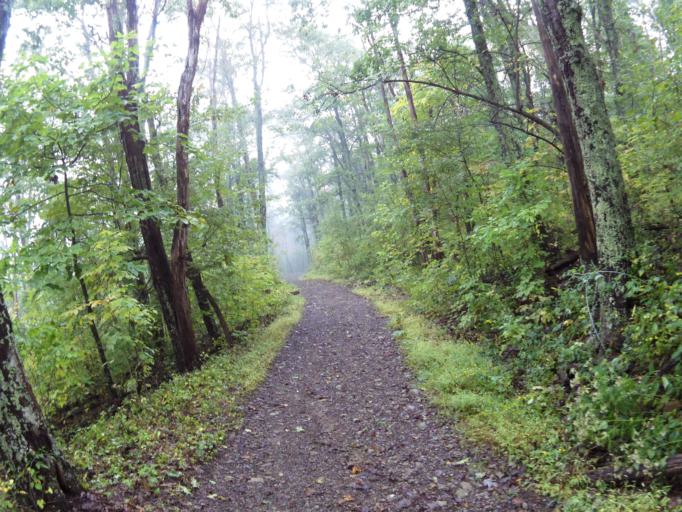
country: US
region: Virginia
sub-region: Rappahannock County
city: Washington
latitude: 38.7679
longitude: -78.2967
